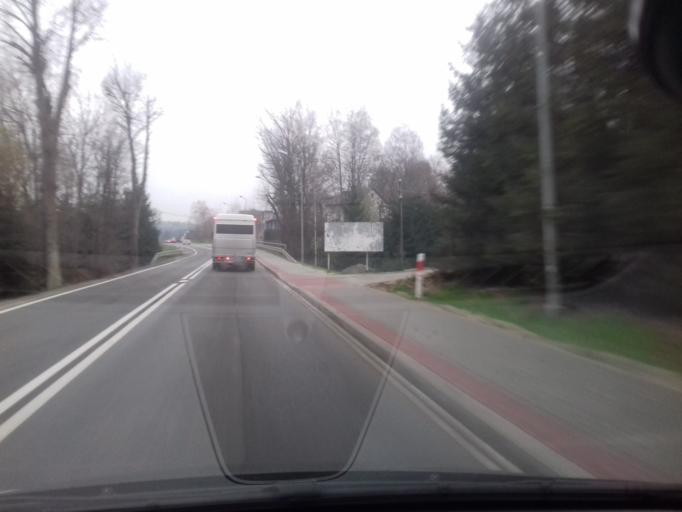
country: PL
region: Lesser Poland Voivodeship
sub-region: Powiat limanowski
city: Limanowa
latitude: 49.7195
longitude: 20.3885
